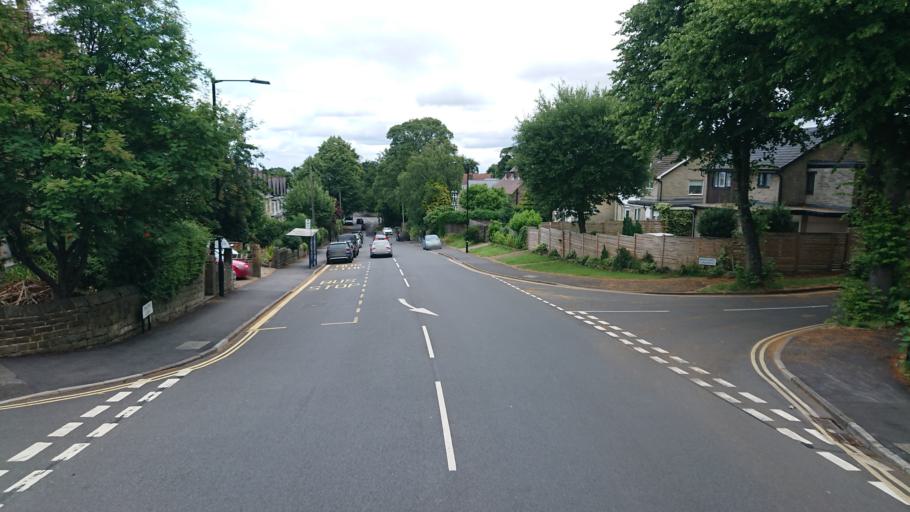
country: GB
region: England
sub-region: Sheffield
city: Sheffield
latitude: 53.3633
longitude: -1.5046
